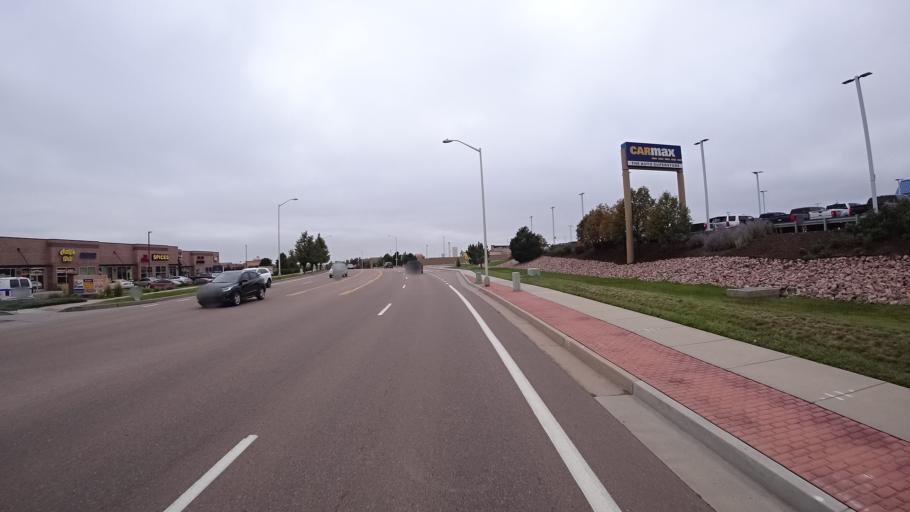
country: US
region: Colorado
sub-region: El Paso County
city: Cimarron Hills
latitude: 38.8905
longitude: -104.7149
